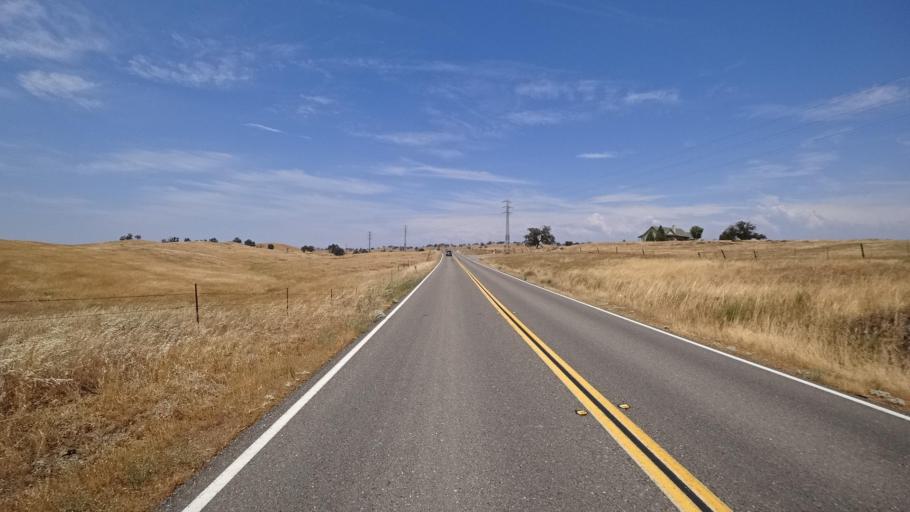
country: US
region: California
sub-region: Merced County
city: Planada
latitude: 37.5321
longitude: -120.3286
